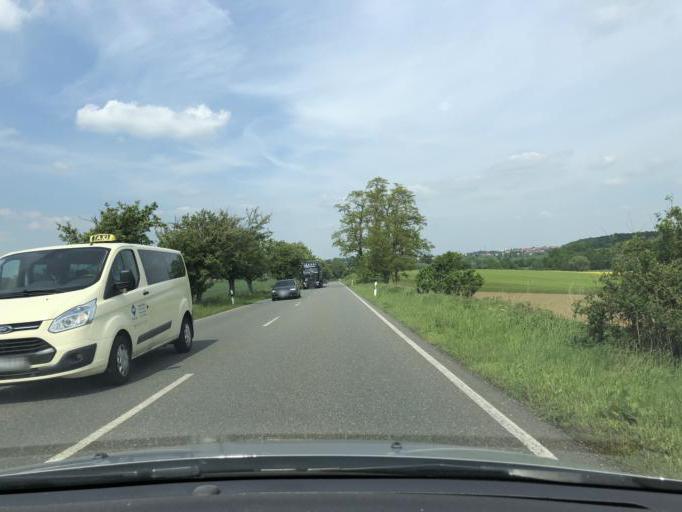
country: DE
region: Thuringia
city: Altenburg
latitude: 50.9651
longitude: 12.4141
